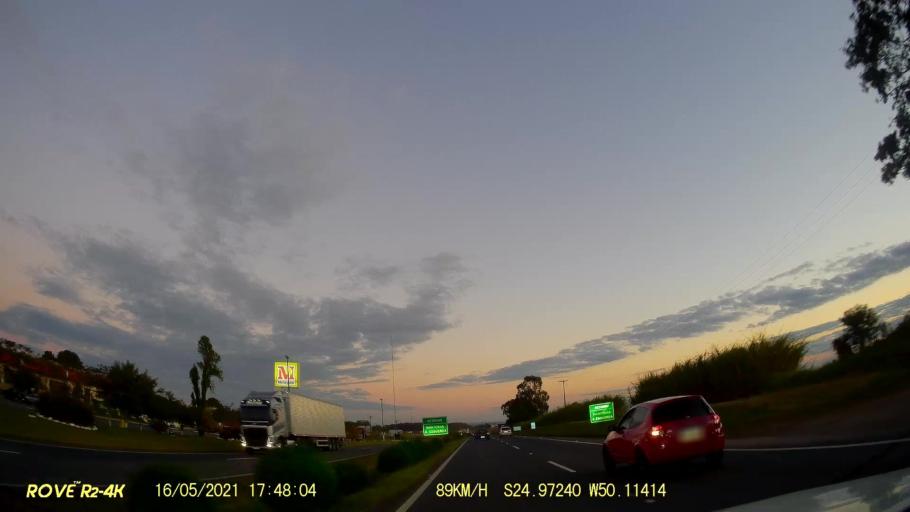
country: BR
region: Parana
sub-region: Carambei
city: Carambei
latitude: -24.9726
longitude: -50.1142
